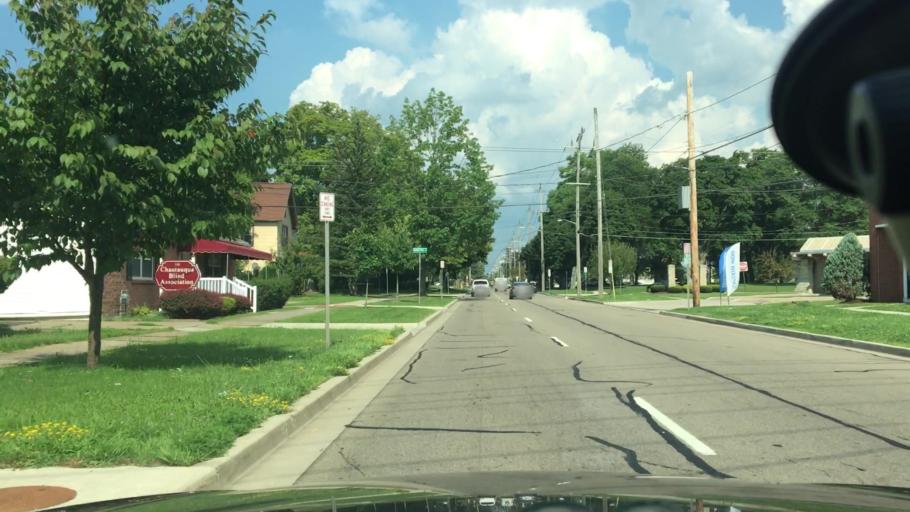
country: US
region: New York
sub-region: Chautauqua County
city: Jamestown
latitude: 42.0970
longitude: -79.2488
